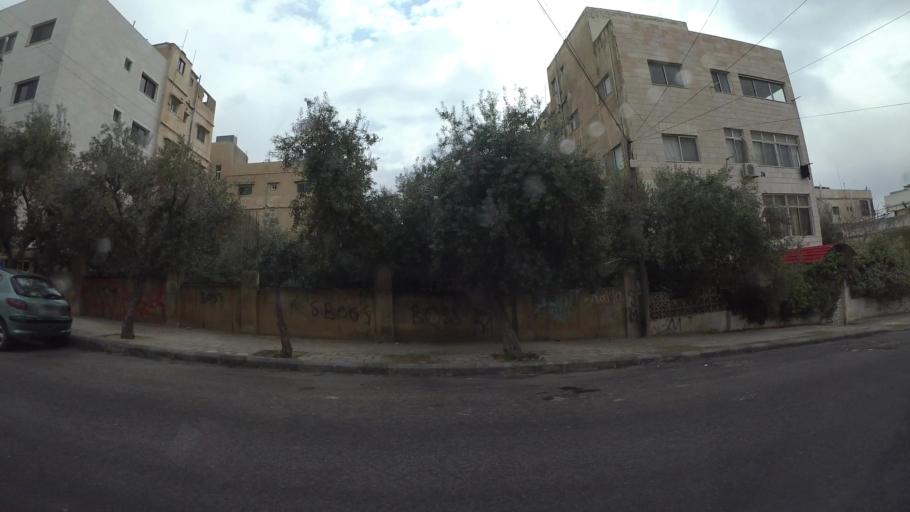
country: JO
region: Amman
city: Amman
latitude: 31.9809
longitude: 35.9273
